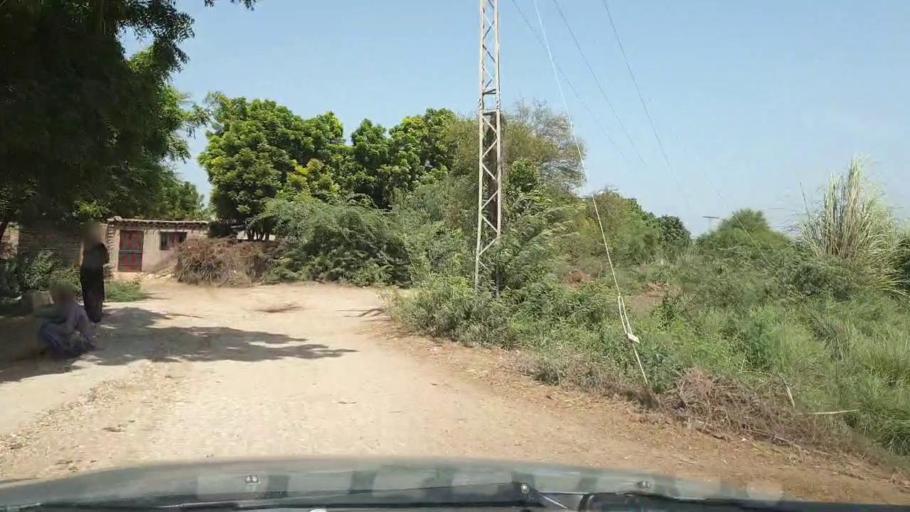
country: PK
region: Sindh
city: Tando Muhammad Khan
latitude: 25.1779
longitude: 68.6311
